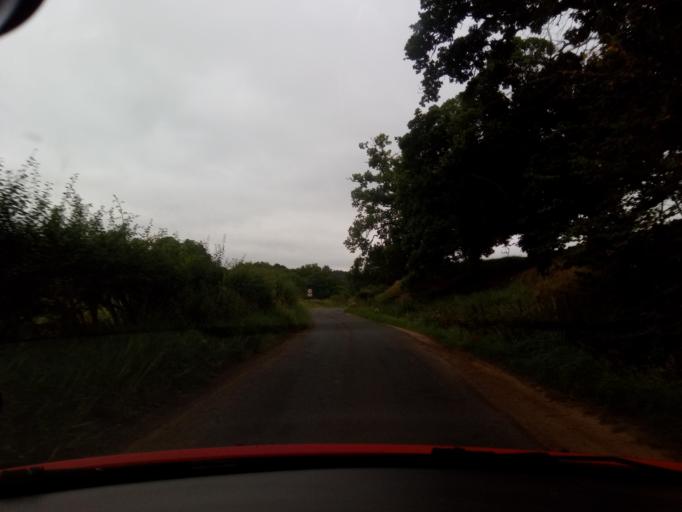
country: GB
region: England
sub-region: Northumberland
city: Otterburn
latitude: 55.3206
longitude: -2.0702
